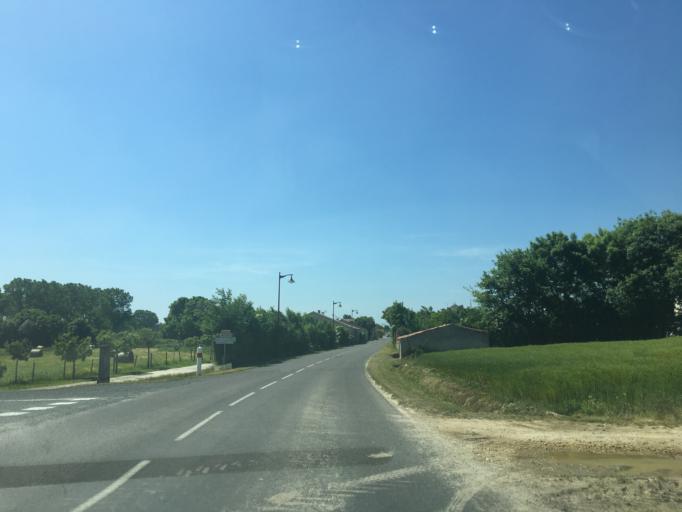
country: FR
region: Poitou-Charentes
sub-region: Departement des Deux-Sevres
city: Beauvoir-sur-Niort
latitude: 46.0797
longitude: -0.5349
